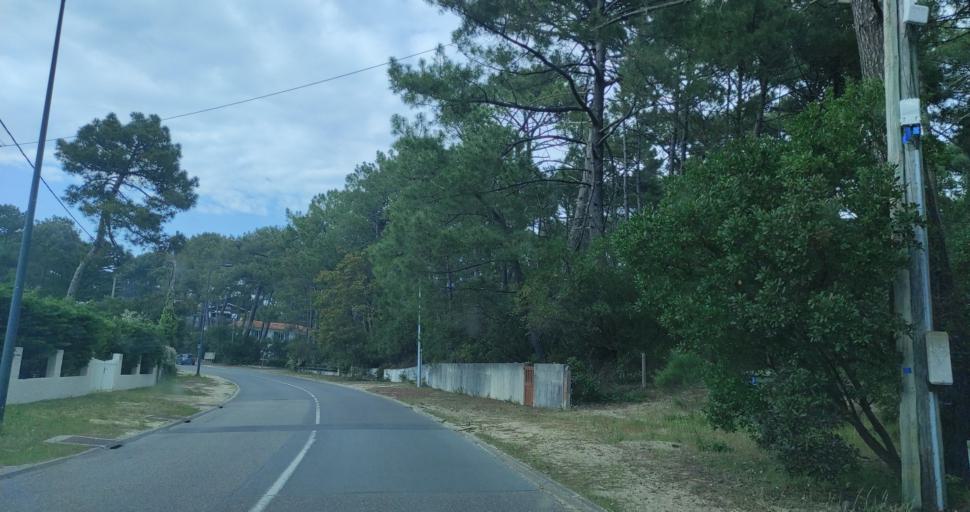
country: FR
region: Aquitaine
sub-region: Departement de la Gironde
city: Arcachon
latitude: 44.6664
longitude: -1.2426
